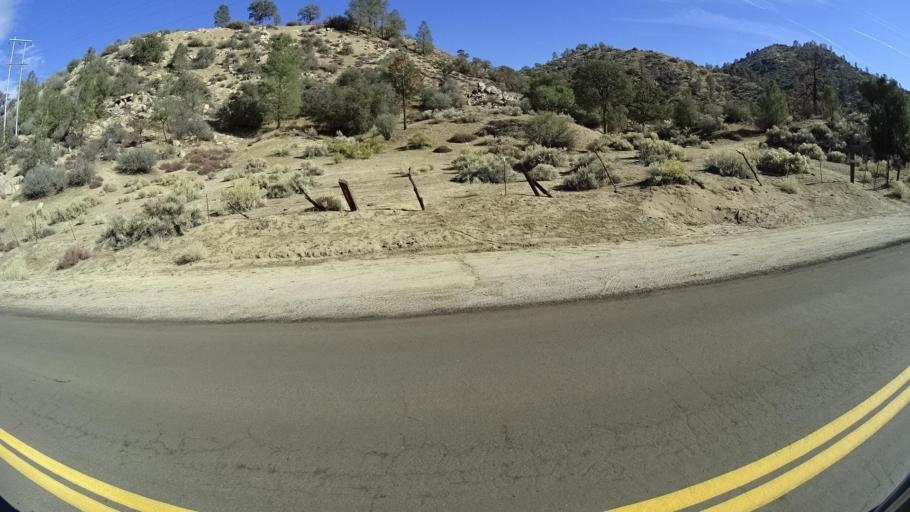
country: US
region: California
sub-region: Kern County
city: Bodfish
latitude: 35.5309
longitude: -118.5121
